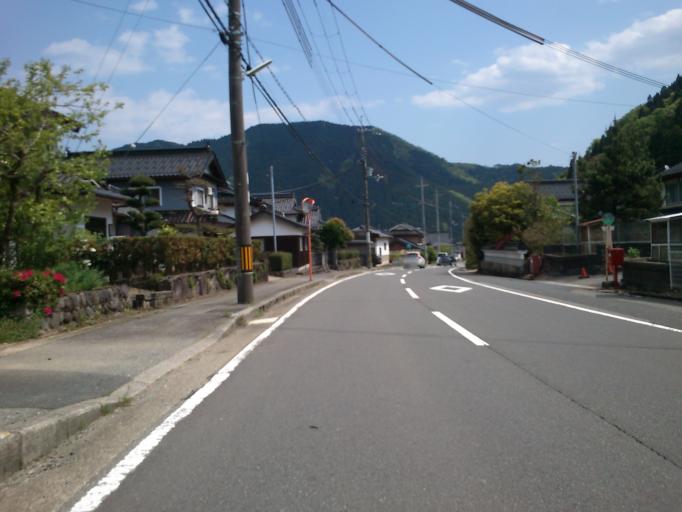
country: JP
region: Kyoto
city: Fukuchiyama
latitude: 35.3543
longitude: 134.9426
